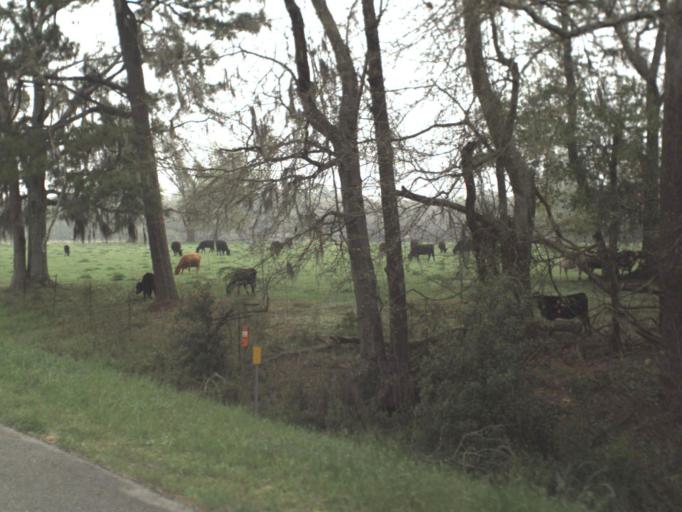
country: US
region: Florida
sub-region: Gadsden County
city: Gretna
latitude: 30.5560
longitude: -84.6770
